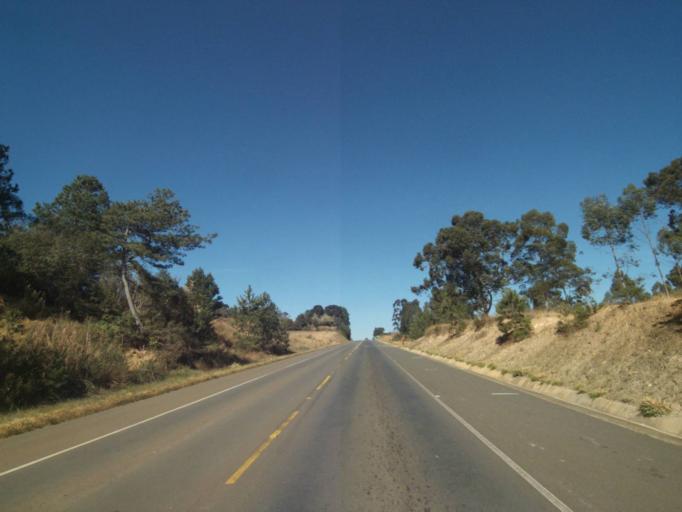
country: BR
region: Parana
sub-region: Tibagi
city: Tibagi
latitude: -24.5952
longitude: -50.4375
